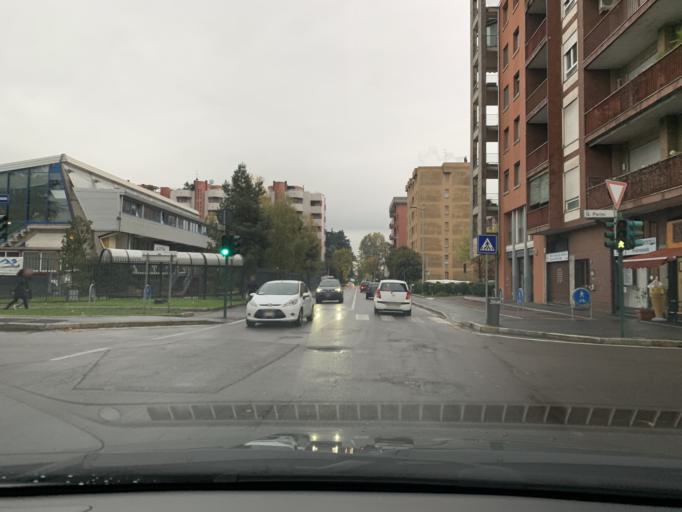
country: IT
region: Lombardy
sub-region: Provincia di Varese
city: Saronno
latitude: 45.6260
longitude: 9.0463
